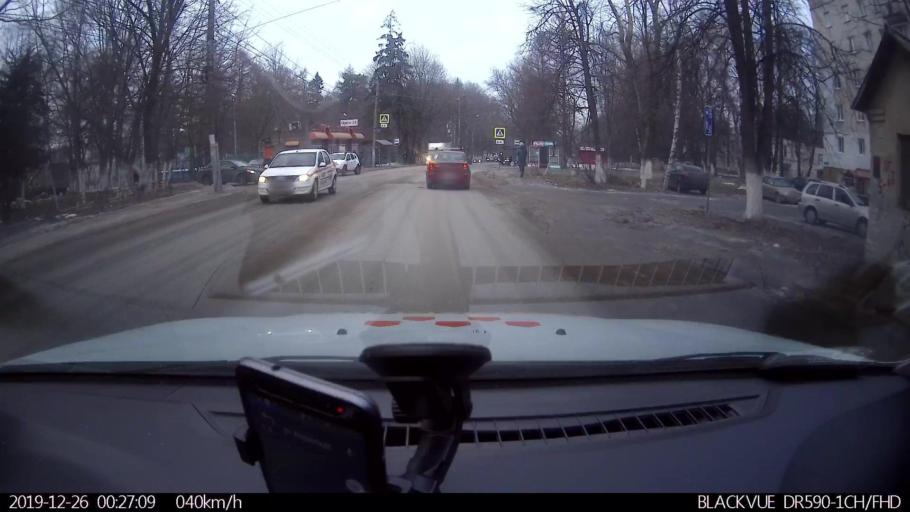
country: RU
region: Nizjnij Novgorod
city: Nizhniy Novgorod
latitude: 56.2626
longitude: 44.0001
